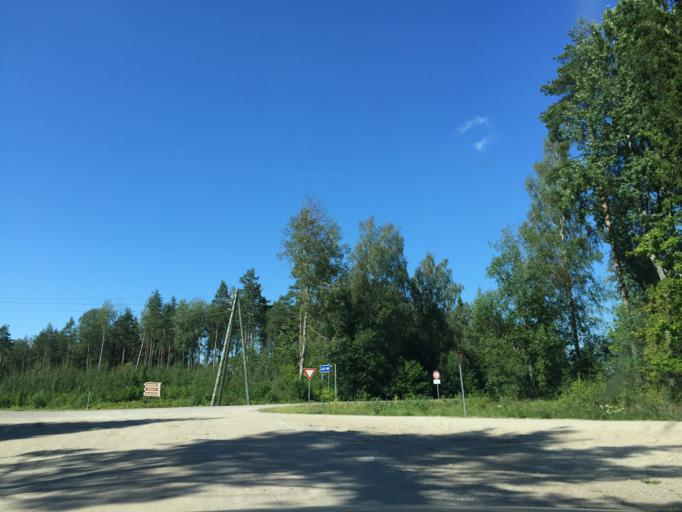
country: LV
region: Limbazu Rajons
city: Limbazi
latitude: 57.4223
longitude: 24.7063
